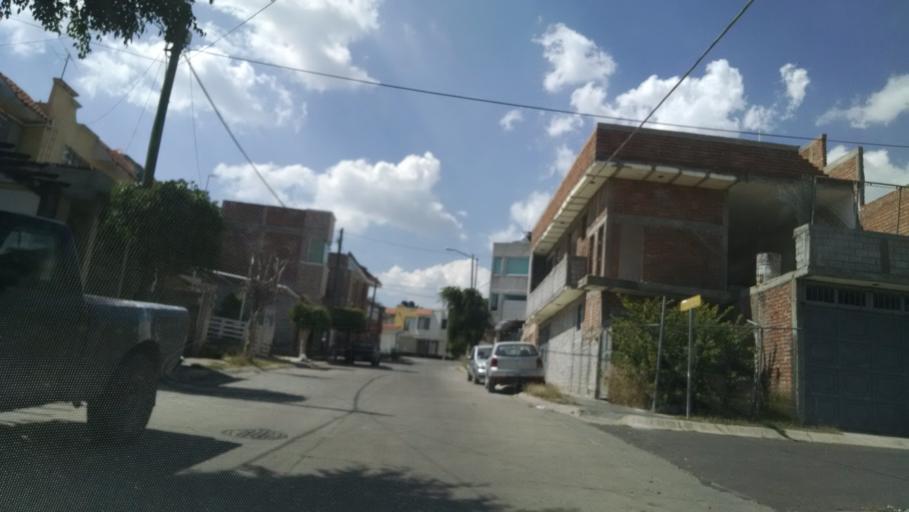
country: MX
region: Guanajuato
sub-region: Leon
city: Ejido la Joya
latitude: 21.1209
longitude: -101.7253
